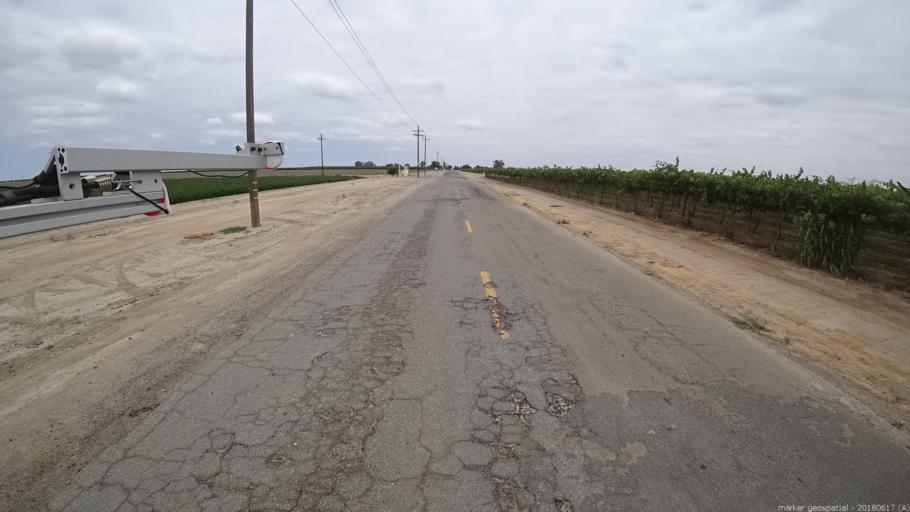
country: US
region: California
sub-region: Madera County
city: Parkwood
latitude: 36.8867
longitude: -120.1650
